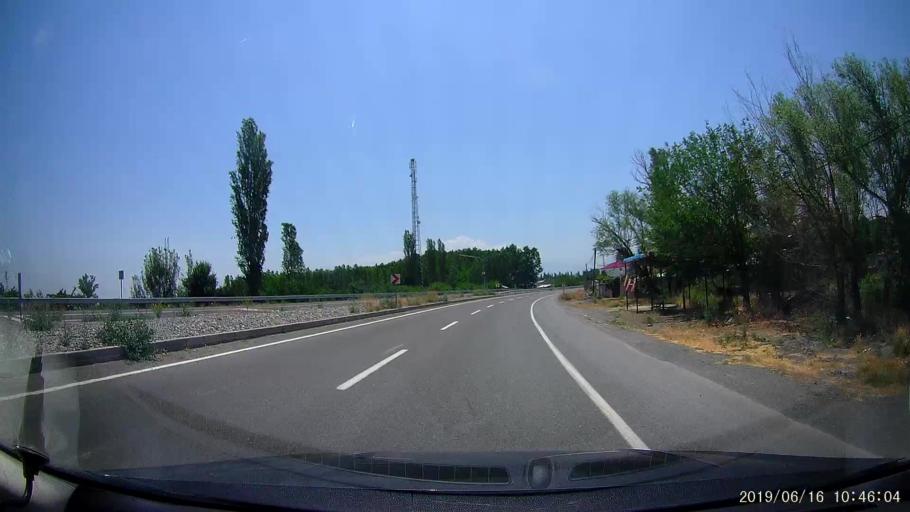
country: AM
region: Armavir
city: Shenavan
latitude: 40.0252
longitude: 43.8765
